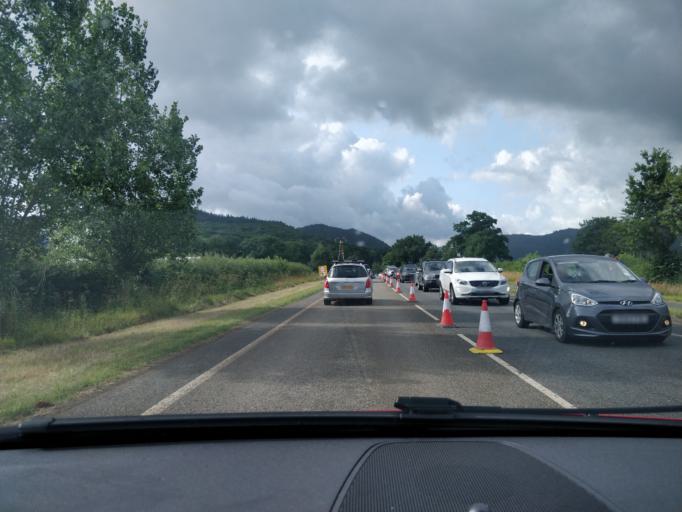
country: GB
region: Wales
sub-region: Conwy
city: Llanrwst
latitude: 53.1125
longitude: -3.7821
